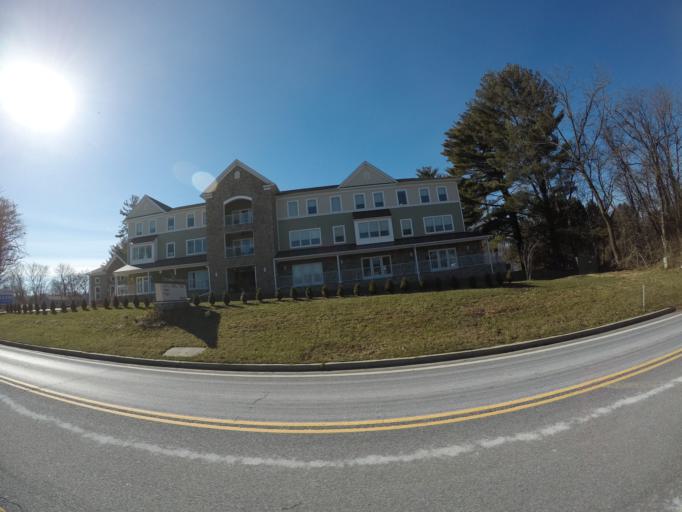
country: US
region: Maryland
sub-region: Howard County
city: Columbia
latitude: 39.2315
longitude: -76.8292
